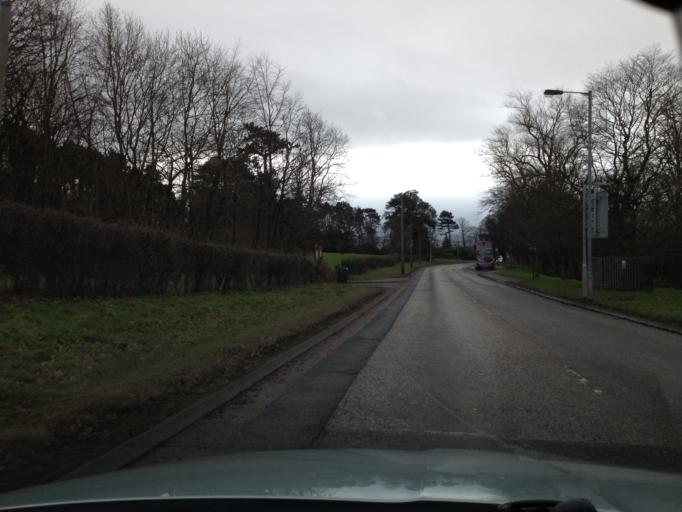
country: GB
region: Scotland
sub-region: Edinburgh
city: Colinton
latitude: 55.9510
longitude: -3.2786
